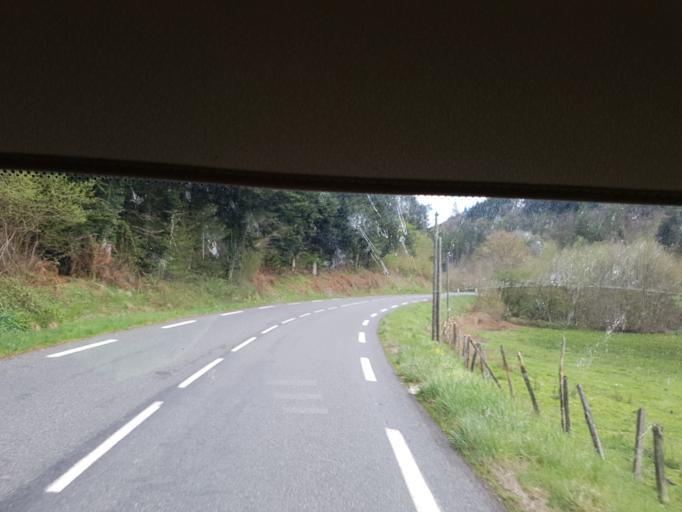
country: FR
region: Rhone-Alpes
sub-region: Departement du Rhone
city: Grandris
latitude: 46.1138
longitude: 4.4654
